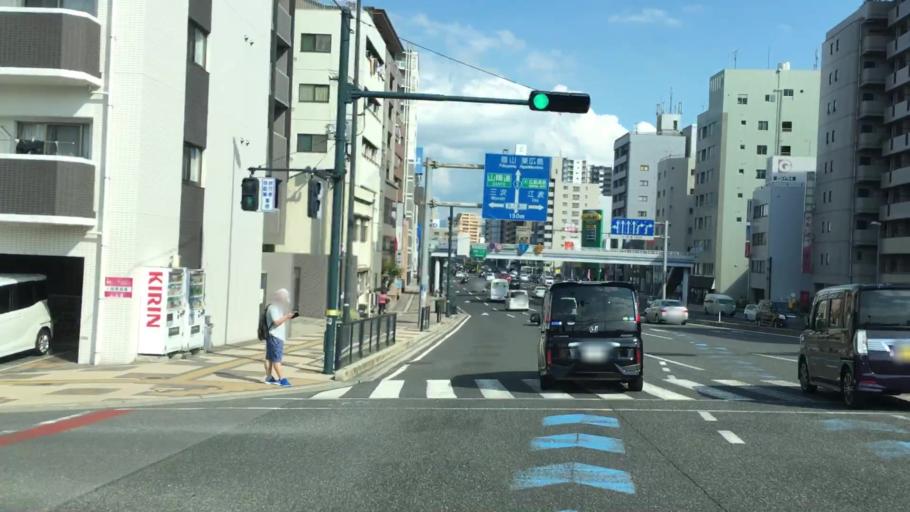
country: JP
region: Hiroshima
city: Hiroshima-shi
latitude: 34.3871
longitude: 132.4410
